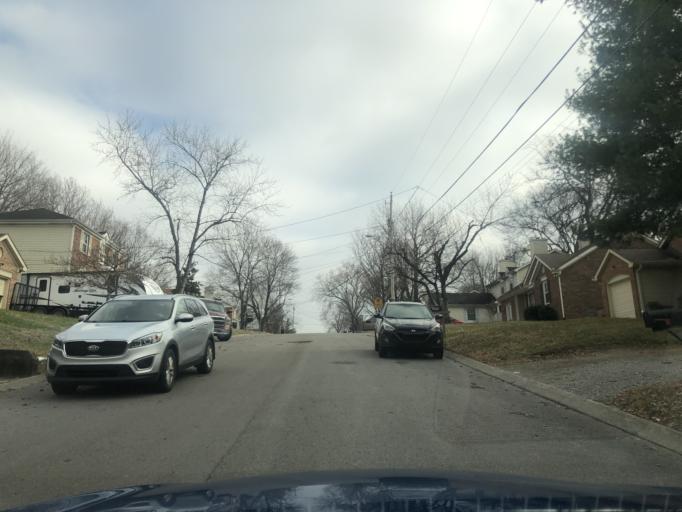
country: US
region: Tennessee
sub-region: Davidson County
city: Oak Hill
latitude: 36.0883
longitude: -86.7100
